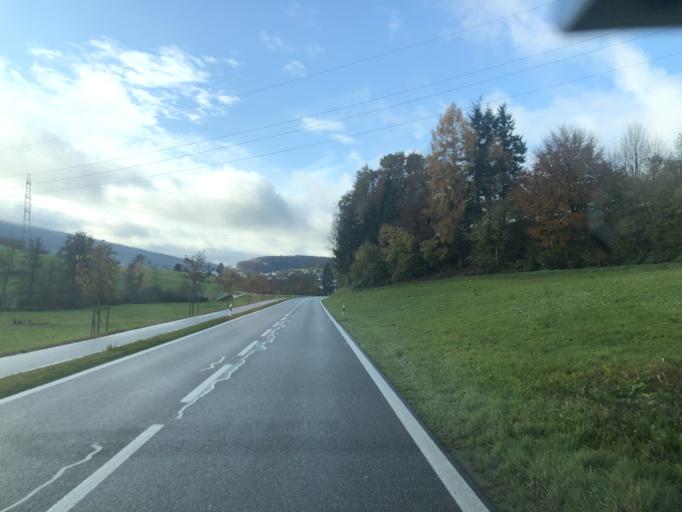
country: CH
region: Aargau
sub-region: Bezirk Baden
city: Unterehrendingen
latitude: 47.5085
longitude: 8.3545
